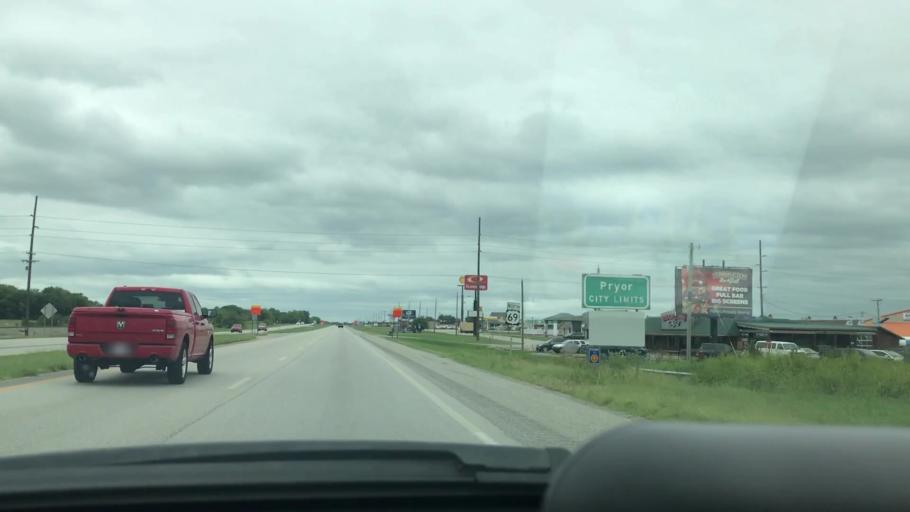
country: US
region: Oklahoma
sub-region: Mayes County
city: Chouteau
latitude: 36.2481
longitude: -95.3360
